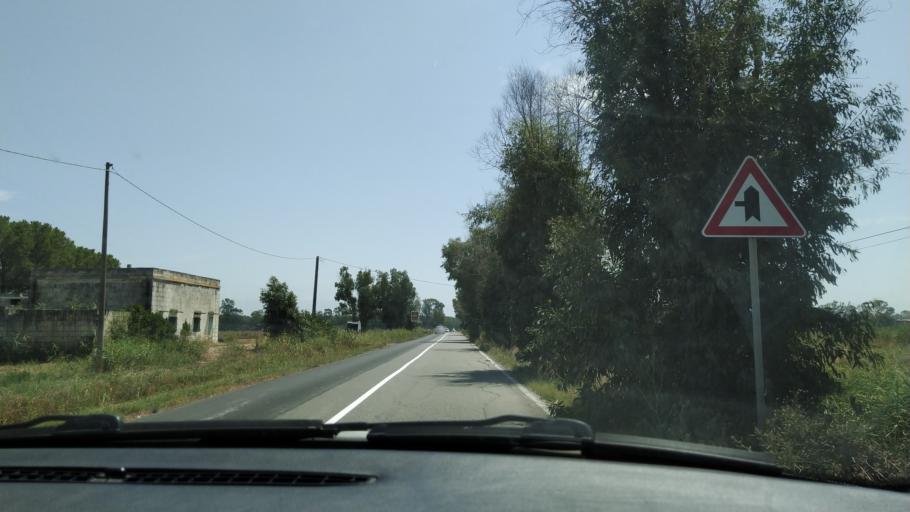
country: IT
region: Basilicate
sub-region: Provincia di Matera
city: Marconia
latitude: 40.3284
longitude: 16.7858
